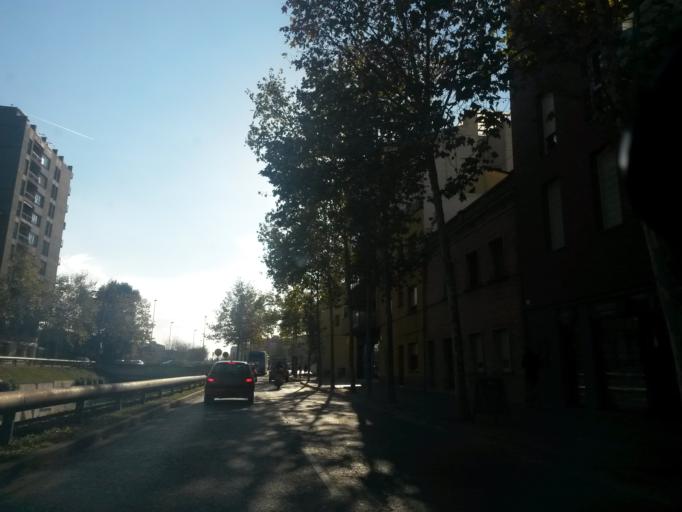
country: ES
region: Catalonia
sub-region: Provincia de Girona
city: Girona
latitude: 41.9776
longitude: 2.8102
